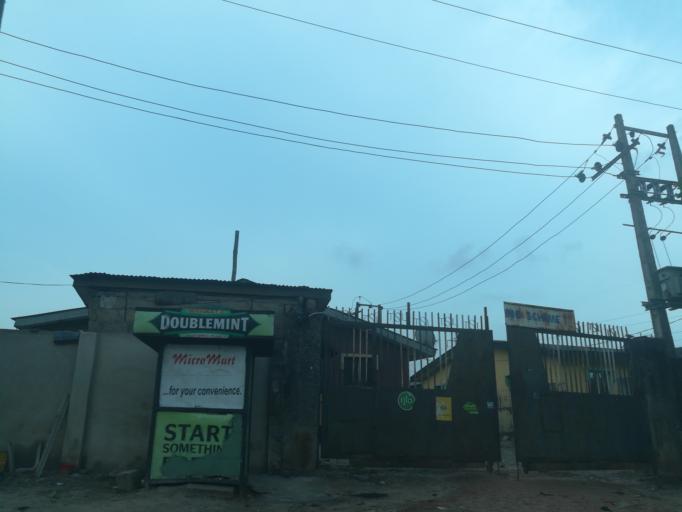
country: NG
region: Lagos
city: Ebute Ikorodu
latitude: 6.6243
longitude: 3.4806
